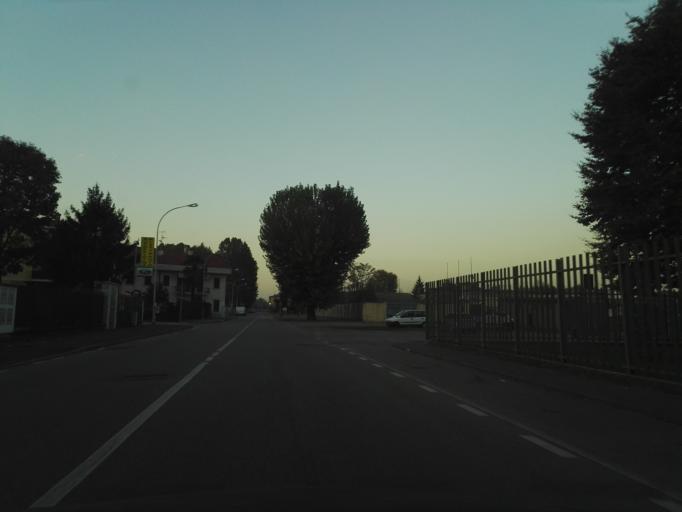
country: IT
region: Lombardy
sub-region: Citta metropolitana di Milano
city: Mezzate
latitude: 45.4414
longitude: 9.2947
